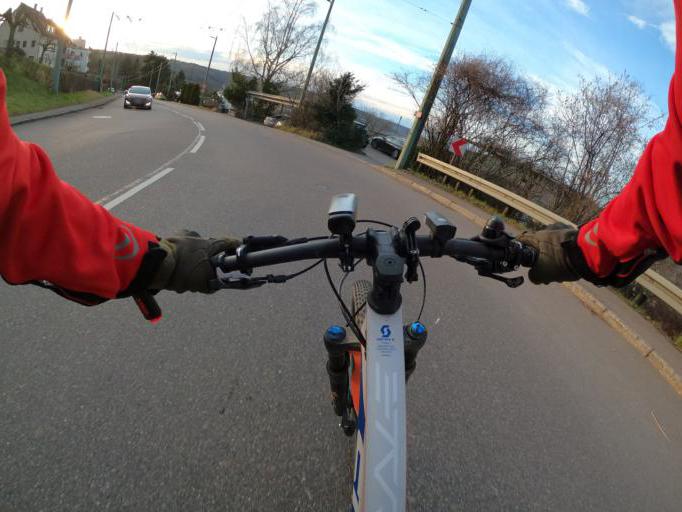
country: DE
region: Baden-Wuerttemberg
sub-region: Regierungsbezirk Stuttgart
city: Esslingen
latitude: 48.7299
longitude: 9.3004
